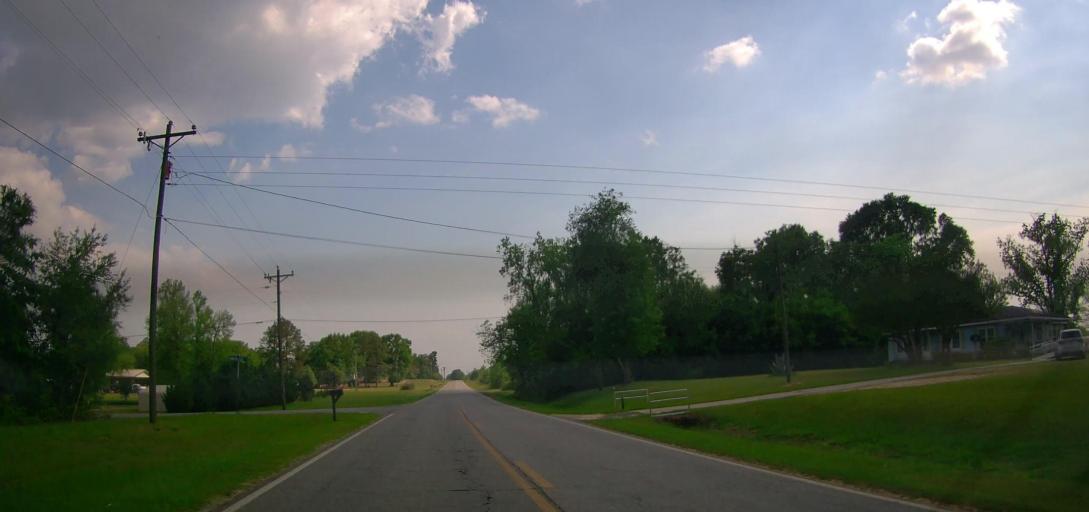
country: US
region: Georgia
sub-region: Laurens County
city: East Dublin
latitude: 32.5964
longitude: -82.8657
